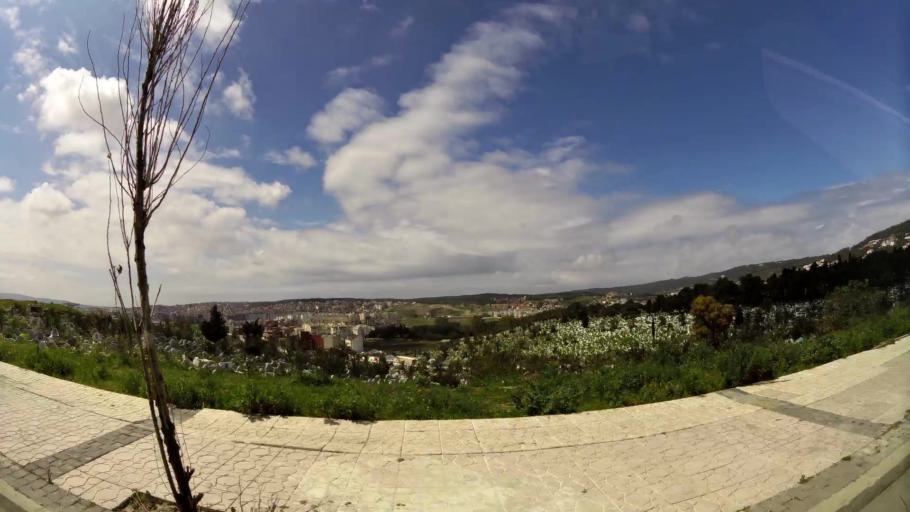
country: MA
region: Tanger-Tetouan
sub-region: Tanger-Assilah
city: Tangier
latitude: 35.7723
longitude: -5.8404
